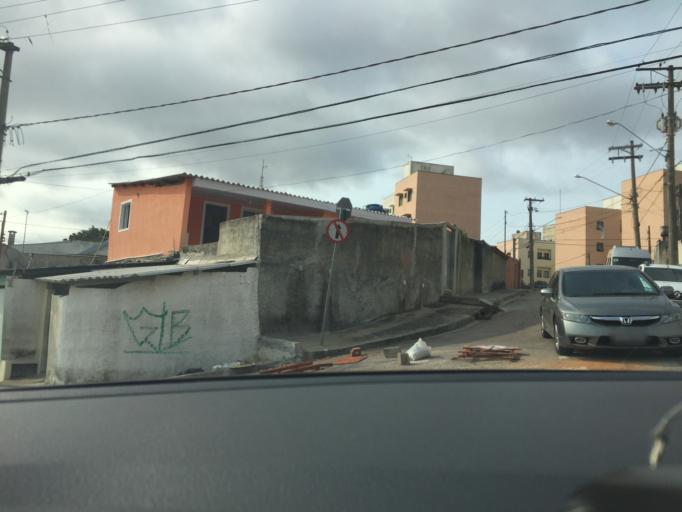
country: BR
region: Sao Paulo
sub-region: Jundiai
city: Jundiai
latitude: -23.2050
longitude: -46.8972
